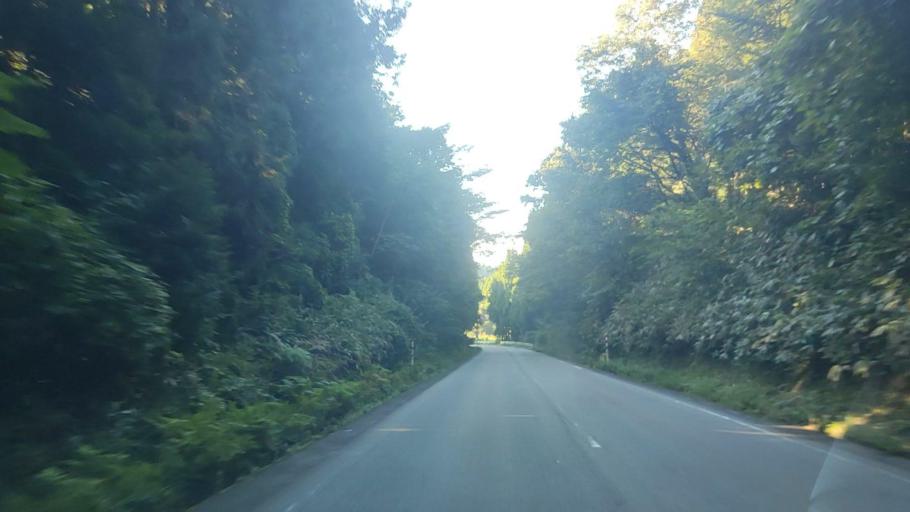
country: JP
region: Ishikawa
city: Nanao
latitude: 37.1229
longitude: 136.9350
